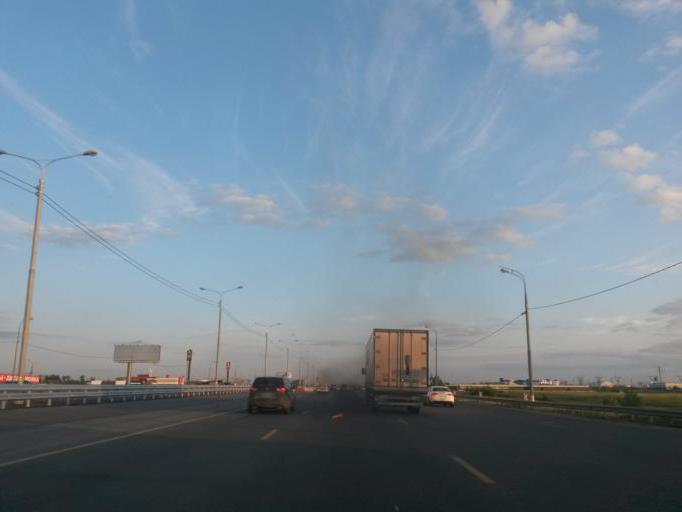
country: RU
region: Moskovskaya
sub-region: Podol'skiy Rayon
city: Podol'sk
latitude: 55.4480
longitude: 37.6172
